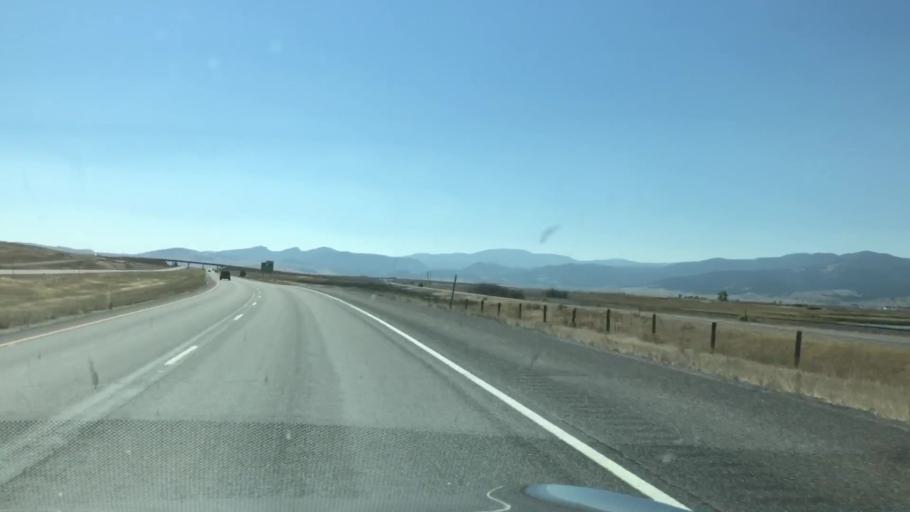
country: US
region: Montana
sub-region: Deer Lodge County
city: Warm Springs
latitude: 46.1160
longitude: -112.7999
